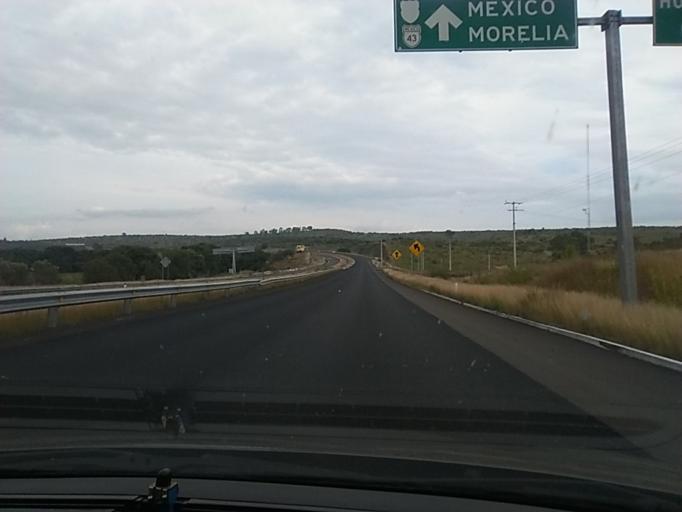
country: MX
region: Mexico
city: Huaniqueo de Morales
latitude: 19.8839
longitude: -101.5121
